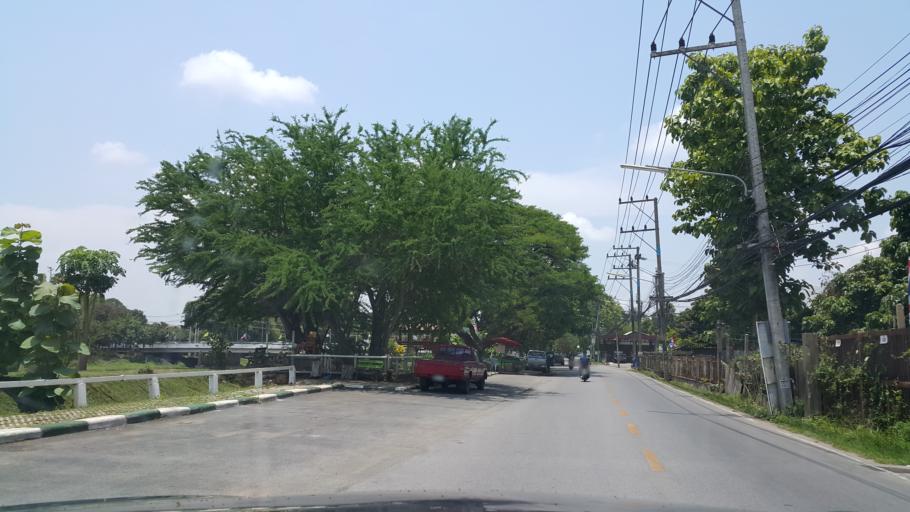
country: TH
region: Chiang Mai
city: Chiang Mai
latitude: 18.8022
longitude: 99.0030
